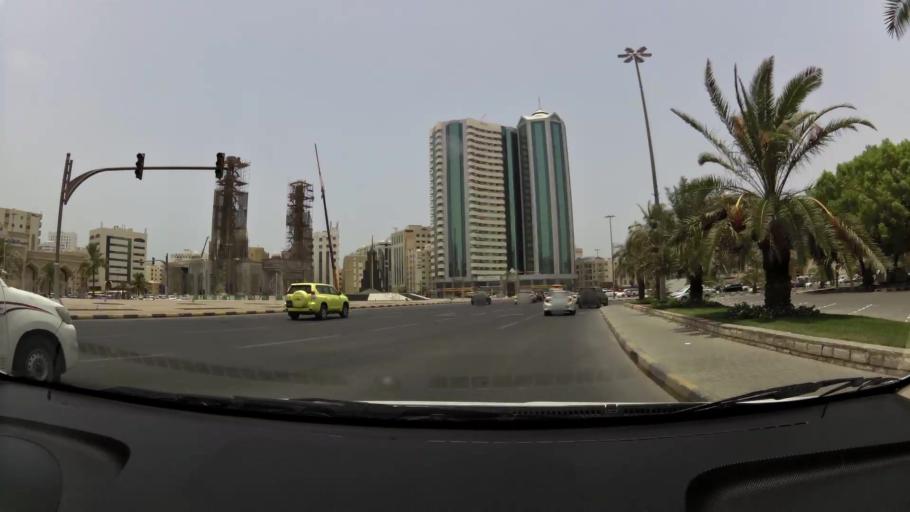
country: AE
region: Ash Shariqah
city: Sharjah
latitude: 25.3521
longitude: 55.3917
